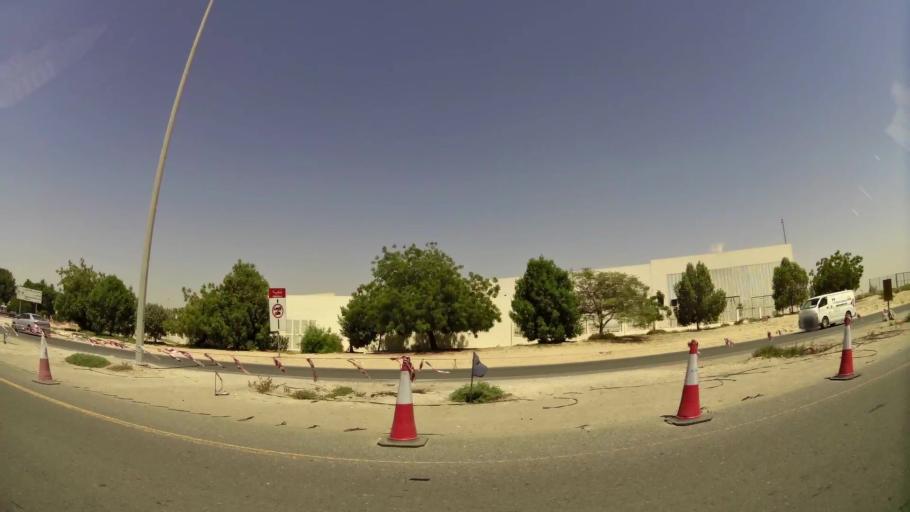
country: AE
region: Dubai
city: Dubai
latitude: 24.9953
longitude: 55.1540
